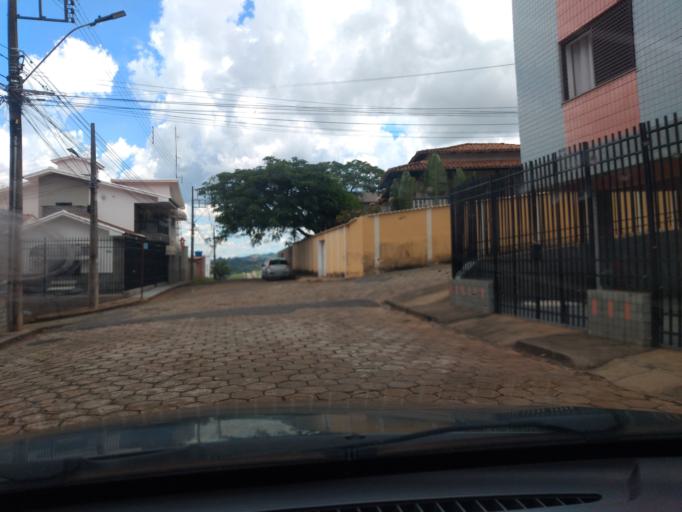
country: BR
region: Minas Gerais
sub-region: Tres Coracoes
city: Tres Coracoes
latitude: -21.6901
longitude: -45.2621
